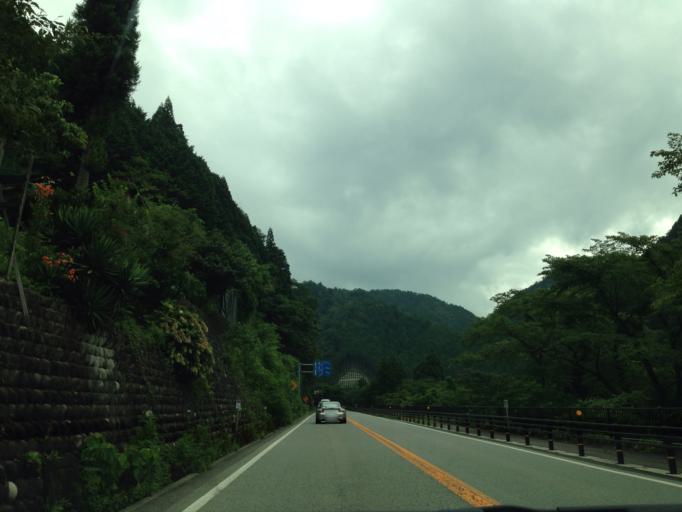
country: JP
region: Gifu
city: Minokamo
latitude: 35.6244
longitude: 137.1760
